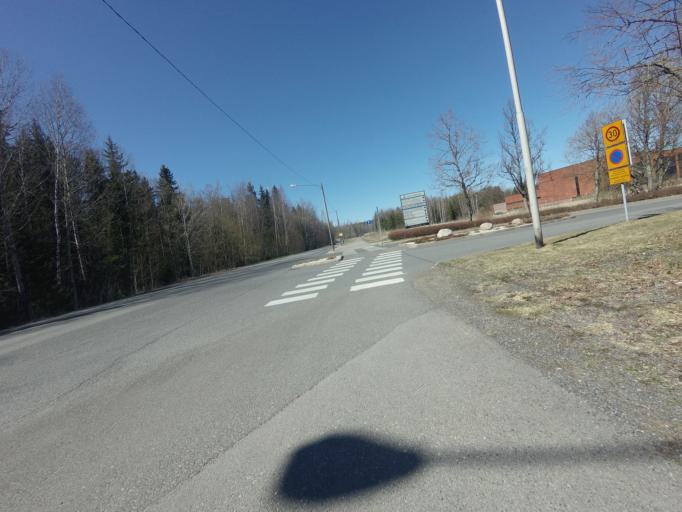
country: FI
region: Varsinais-Suomi
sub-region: Turku
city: Raisio
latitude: 60.4524
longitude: 22.1769
